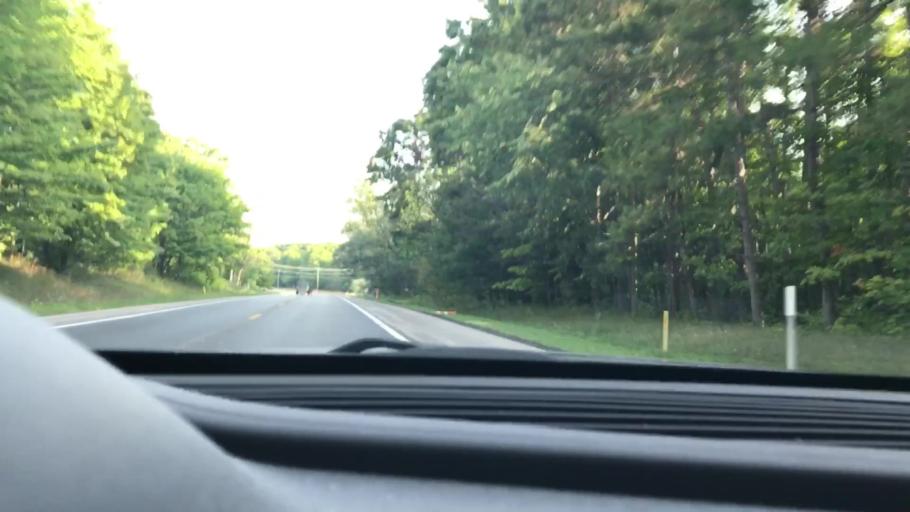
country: US
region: Michigan
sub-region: Antrim County
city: Bellaire
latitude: 45.0512
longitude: -85.3497
